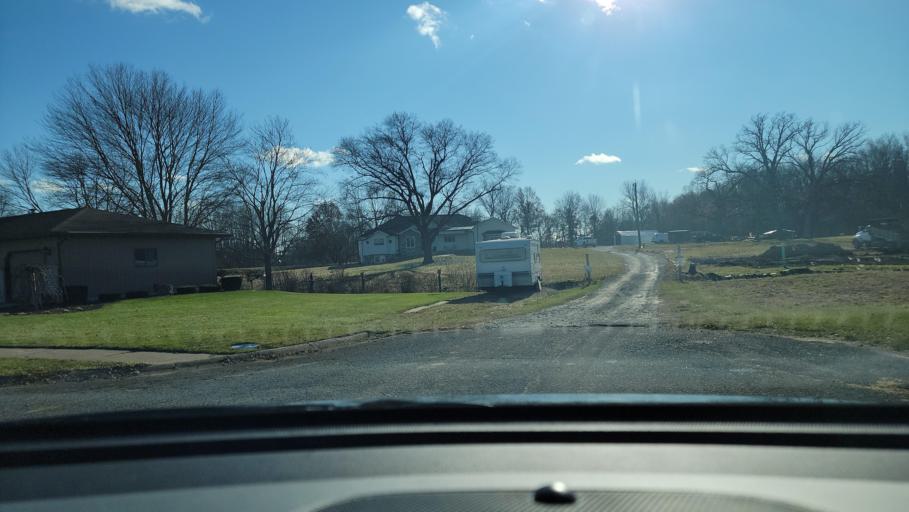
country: US
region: Indiana
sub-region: Porter County
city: Portage
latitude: 41.5629
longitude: -87.1889
